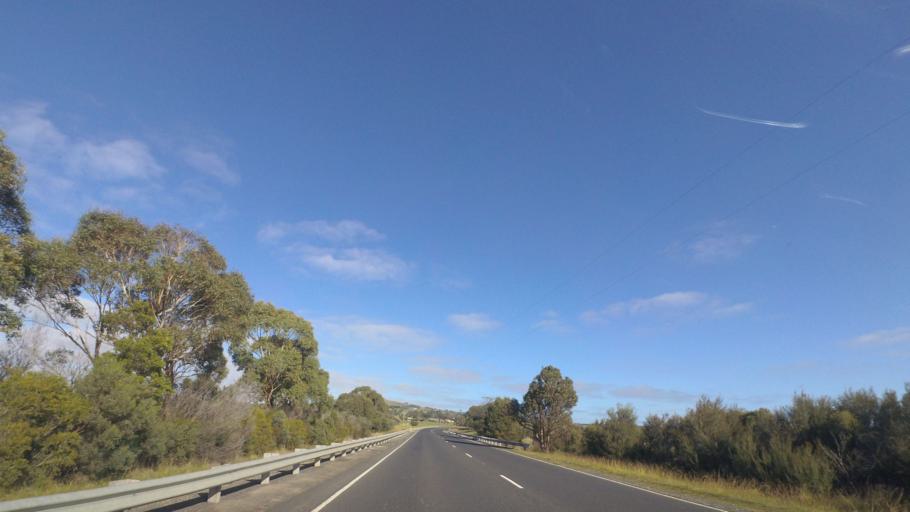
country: AU
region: Victoria
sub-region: Hume
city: Sunbury
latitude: -37.5366
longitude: 144.6577
